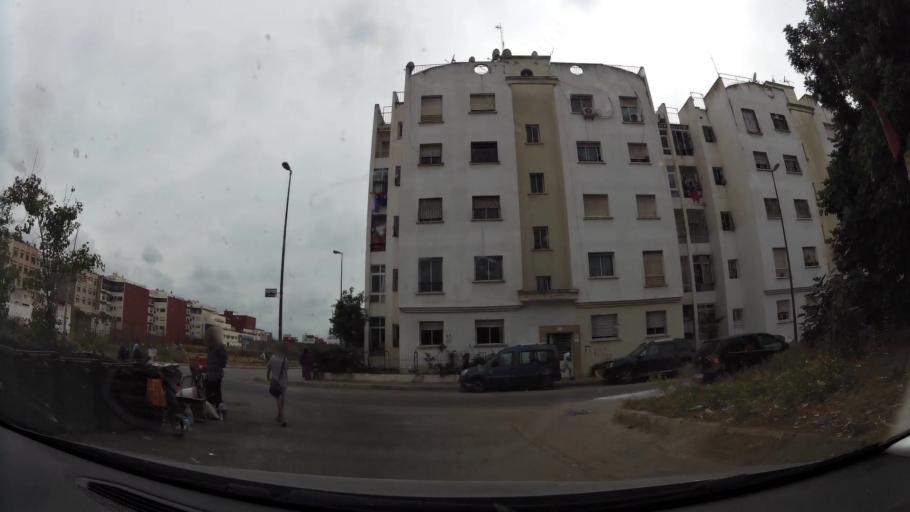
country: MA
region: Rabat-Sale-Zemmour-Zaer
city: Sale
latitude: 34.0432
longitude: -6.8093
